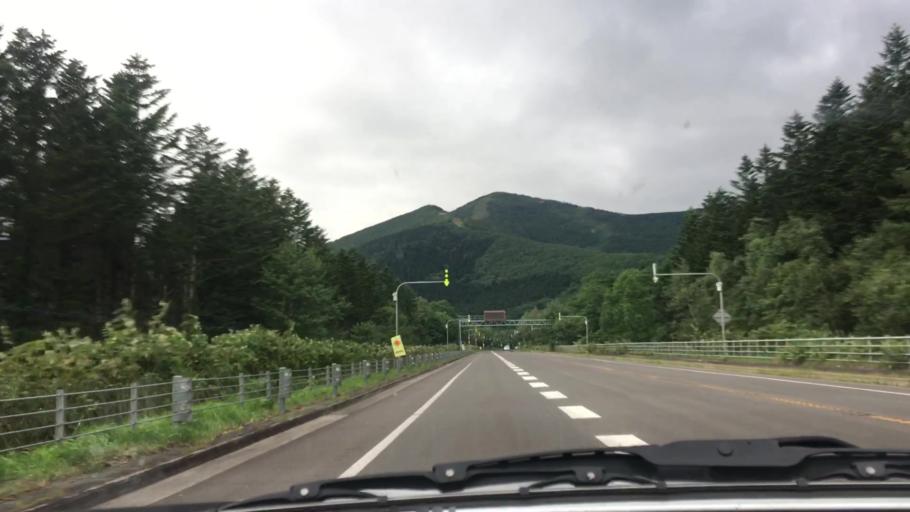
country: JP
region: Hokkaido
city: Otofuke
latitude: 43.1612
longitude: 142.8158
